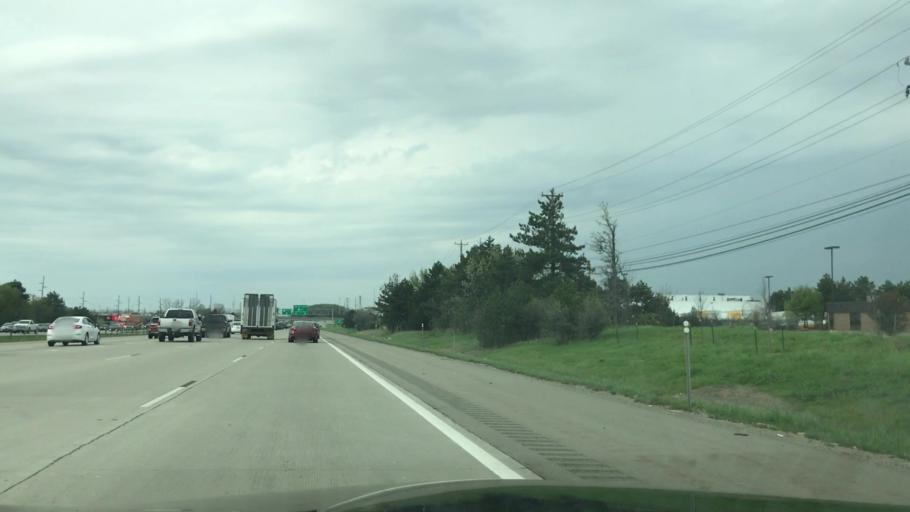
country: US
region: Michigan
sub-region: Oakland County
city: Novi
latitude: 42.4611
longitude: -83.4312
